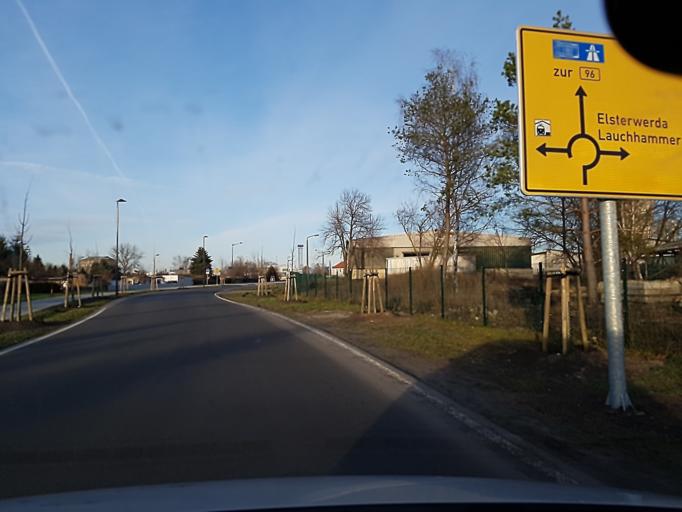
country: DE
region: Brandenburg
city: Finsterwalde
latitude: 51.6303
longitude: 13.7268
